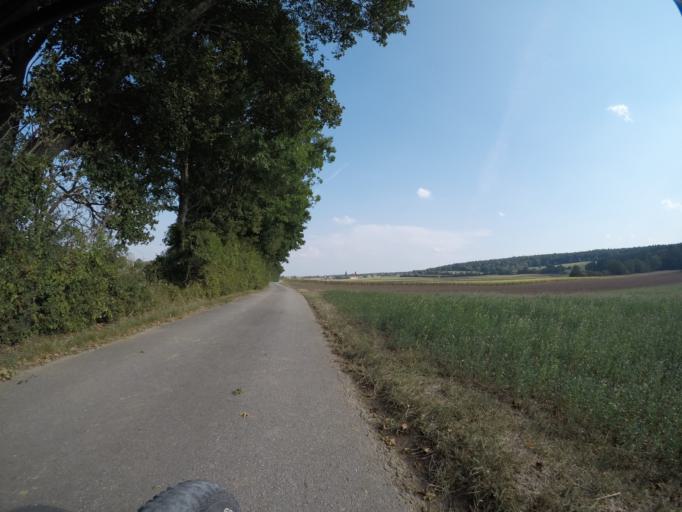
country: AT
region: Lower Austria
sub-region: Politischer Bezirk Baden
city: Hirtenberg
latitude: 47.9638
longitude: 16.1534
